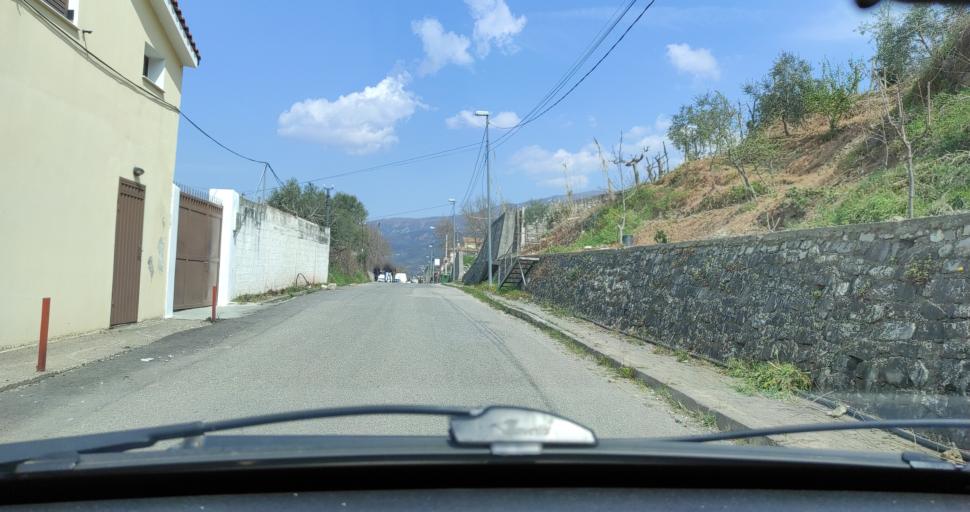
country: AL
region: Lezhe
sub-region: Rrethi i Lezhes
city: Kallmeti i Madh
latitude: 41.8477
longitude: 19.6894
